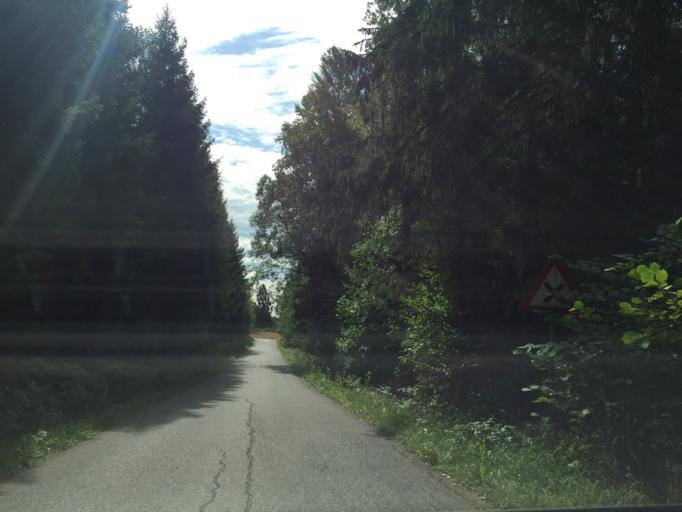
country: NO
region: Akershus
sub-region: Ski
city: Ski
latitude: 59.6524
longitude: 10.8723
